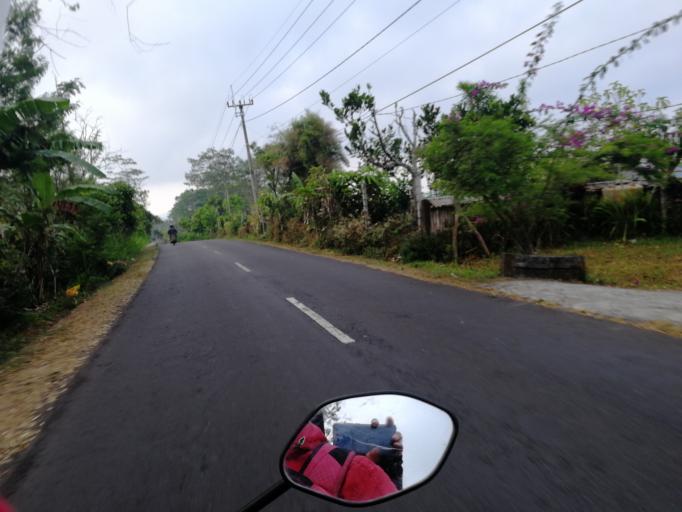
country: ID
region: Bali
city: Peneng
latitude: -8.2489
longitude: 115.2442
